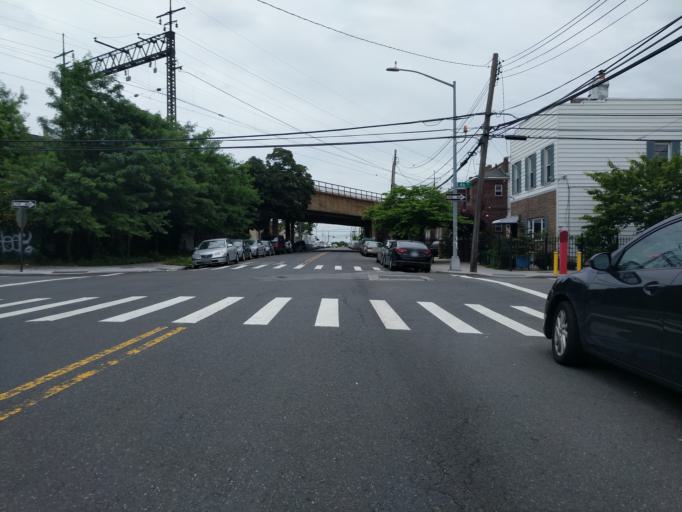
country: US
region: New York
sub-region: Queens County
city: Long Island City
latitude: 40.7658
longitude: -73.9071
